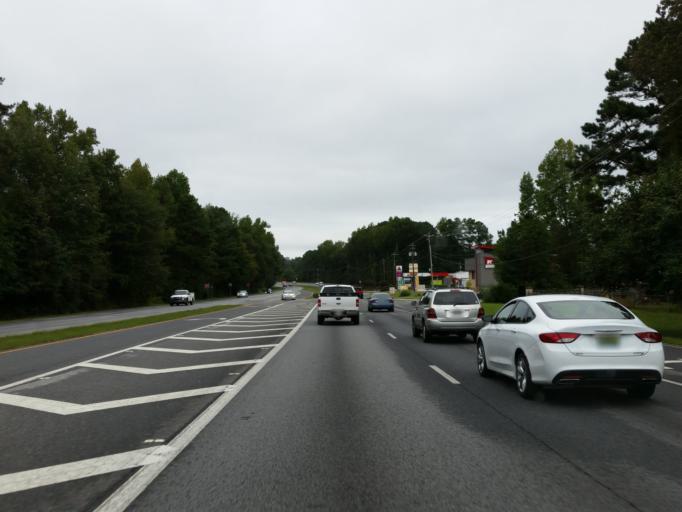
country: US
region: Georgia
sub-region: Clayton County
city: Bonanza
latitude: 33.4696
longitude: -84.3361
